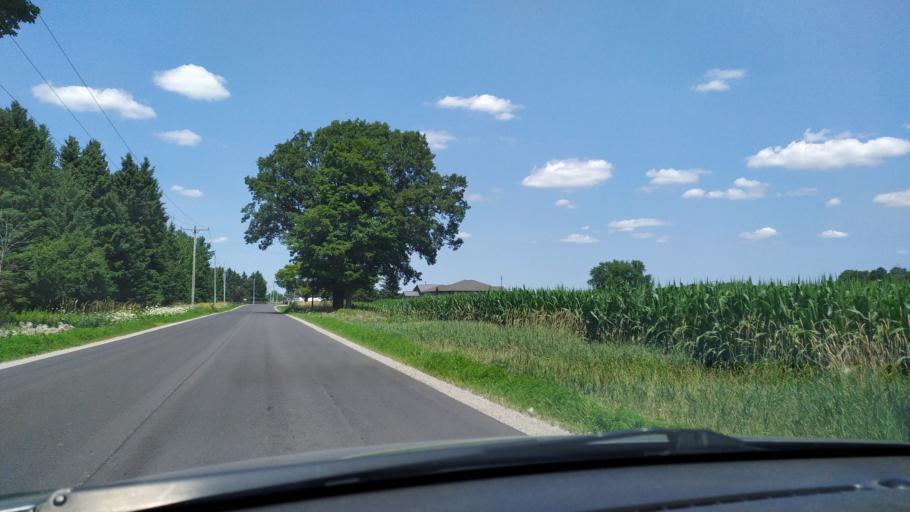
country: CA
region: Ontario
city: Stratford
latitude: 43.3598
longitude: -80.9379
